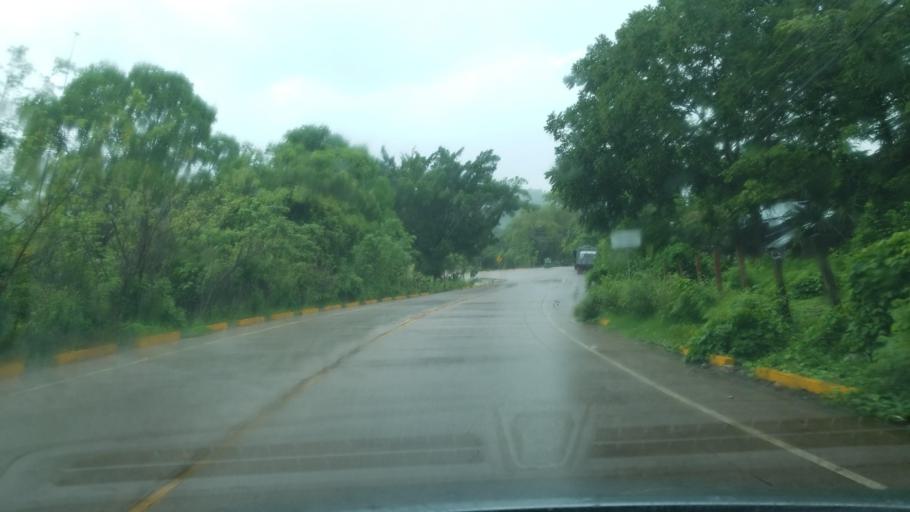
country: HN
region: Copan
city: Copan
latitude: 14.8376
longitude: -89.1512
